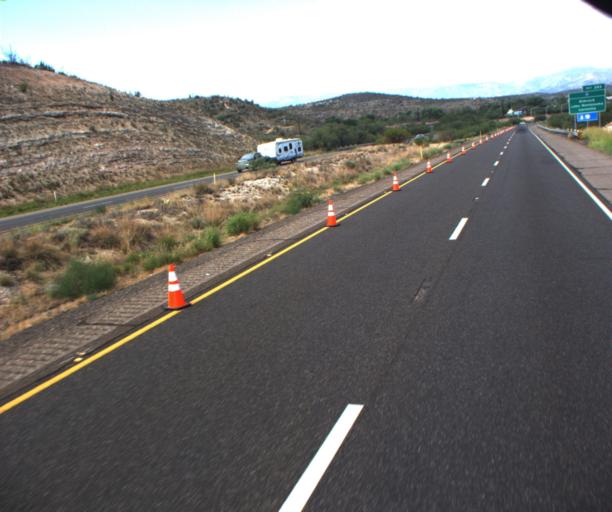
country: US
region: Arizona
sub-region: Yavapai County
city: Lake Montezuma
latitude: 34.6432
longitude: -111.8082
